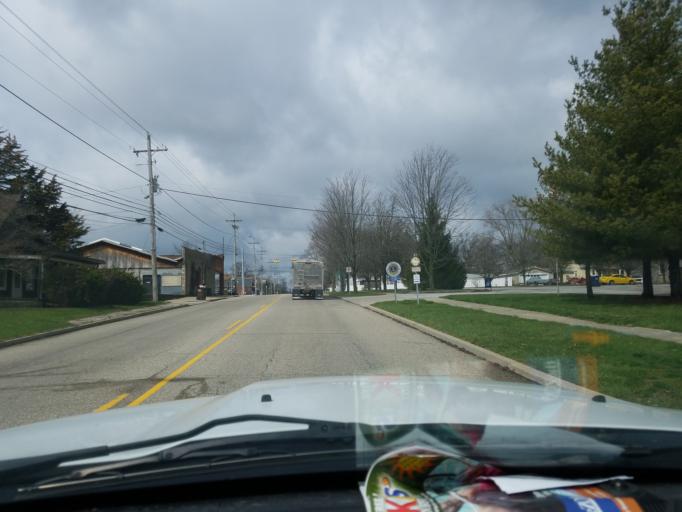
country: US
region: Indiana
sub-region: Vigo County
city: Seelyville
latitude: 39.3903
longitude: -87.2966
